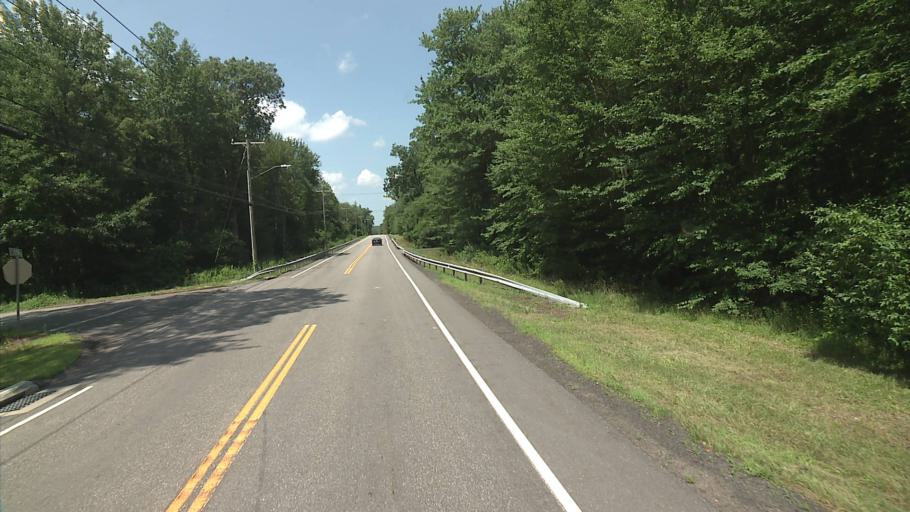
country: US
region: Connecticut
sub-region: Tolland County
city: Tolland
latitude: 41.8199
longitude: -72.3975
